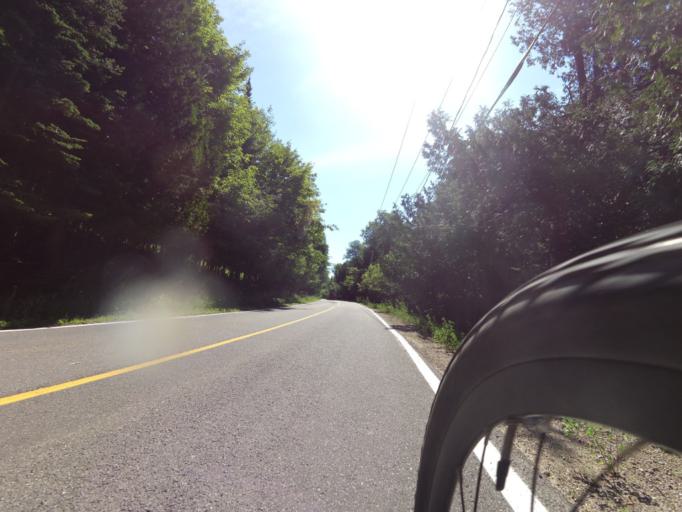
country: CA
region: Quebec
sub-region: Laurentides
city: Brownsburg-Chatham
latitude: 45.8445
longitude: -74.5084
